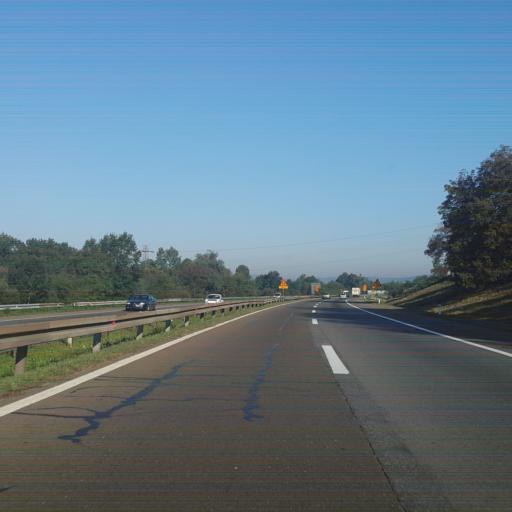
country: RS
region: Central Serbia
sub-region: Belgrade
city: Zvezdara
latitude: 44.6764
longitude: 20.5899
